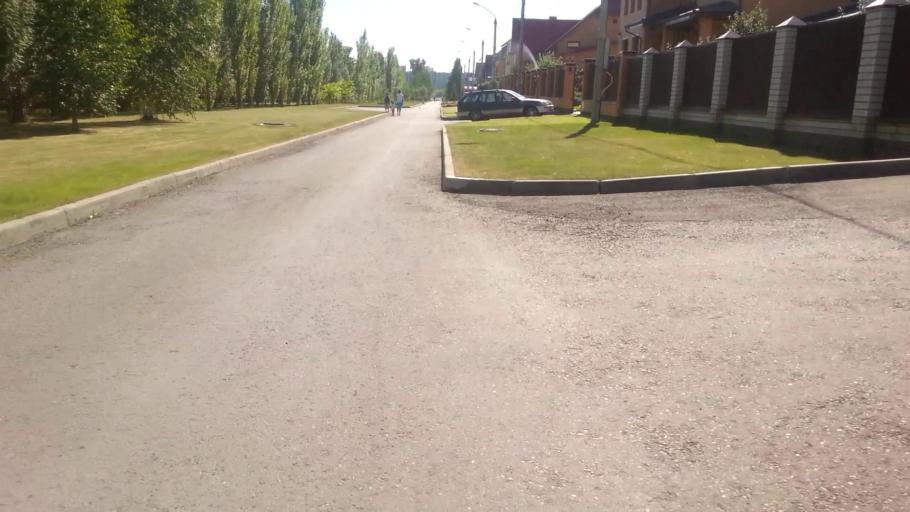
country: RU
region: Altai Krai
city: Novosilikatnyy
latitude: 53.3546
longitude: 83.6560
